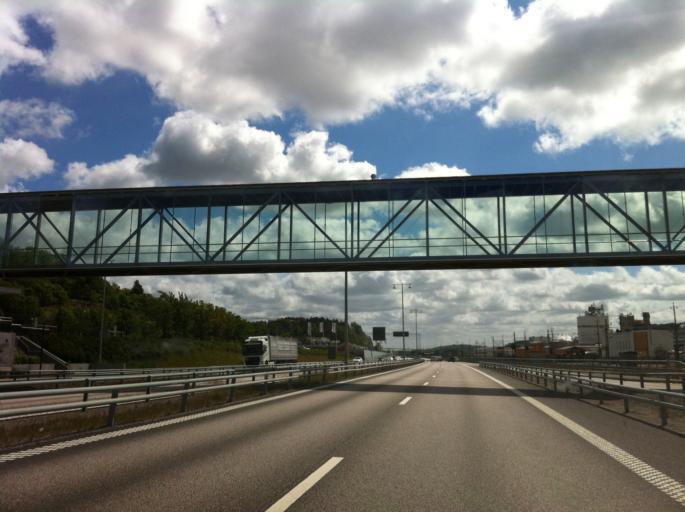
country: SE
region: Vaestra Goetaland
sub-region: Ale Kommun
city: Nodinge-Nol
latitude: 57.8759
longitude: 12.0374
